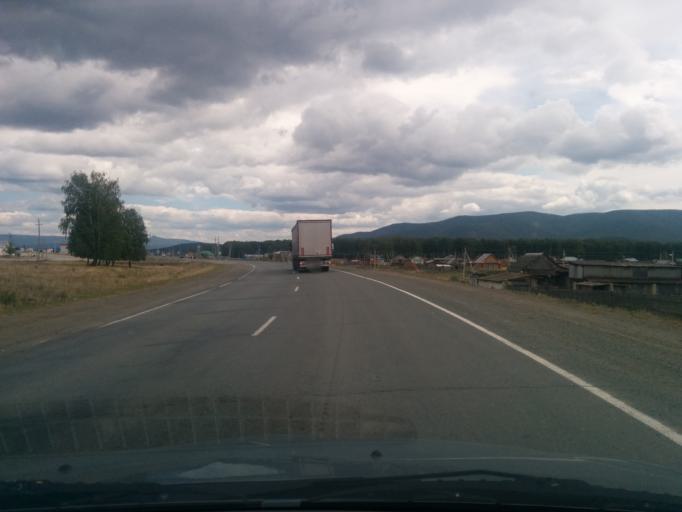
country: RU
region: Bashkortostan
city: Lomovka
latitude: 53.8837
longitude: 58.1002
